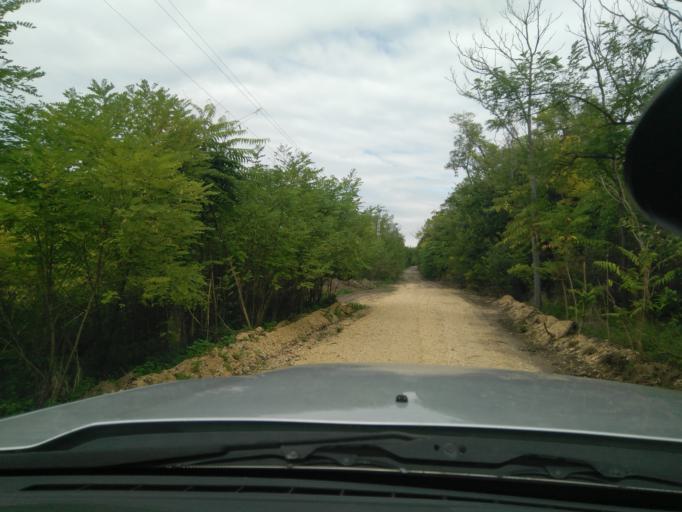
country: HU
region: Fejer
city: Val
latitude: 47.3808
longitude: 18.7407
